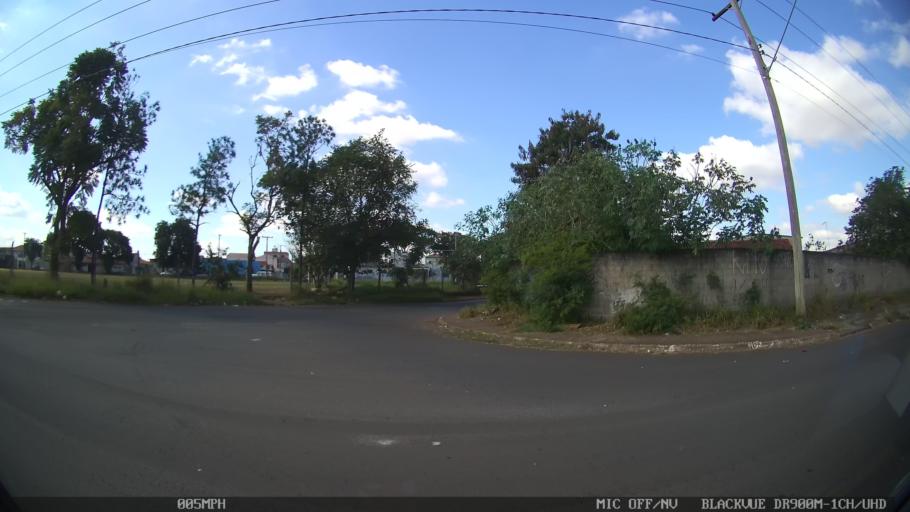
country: BR
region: Sao Paulo
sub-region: Hortolandia
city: Hortolandia
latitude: -22.8775
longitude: -47.2070
